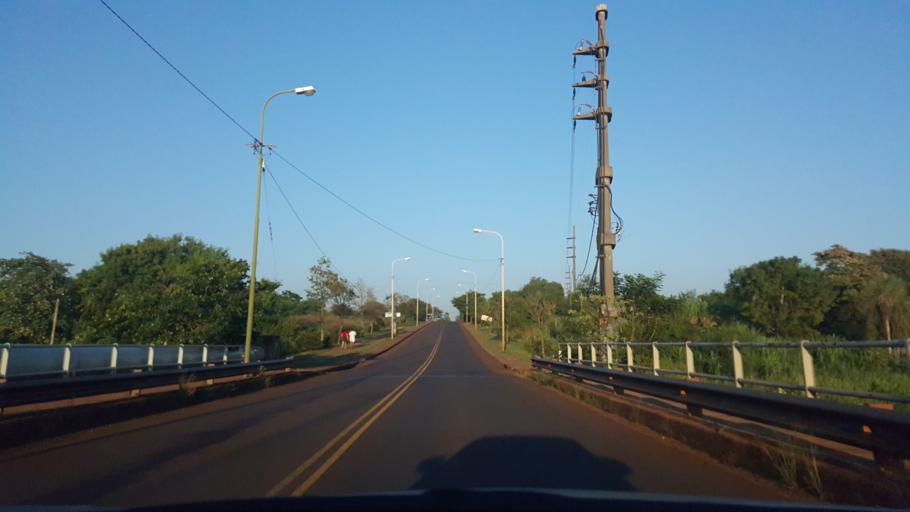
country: AR
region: Misiones
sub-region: Departamento de Capital
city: Posadas
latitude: -27.3726
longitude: -55.9572
